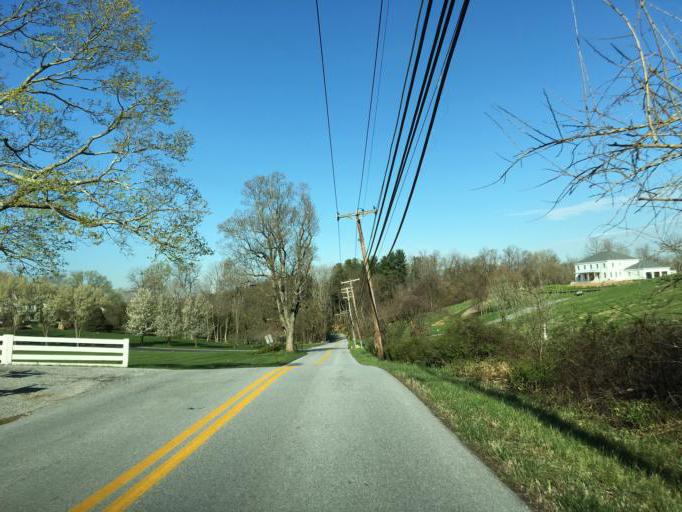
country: US
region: Maryland
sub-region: Baltimore County
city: Hunt Valley
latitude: 39.5430
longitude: -76.6275
